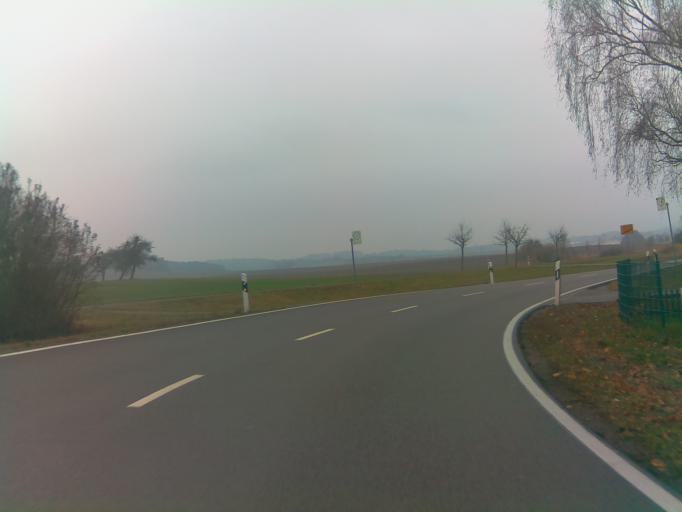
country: DE
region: Thuringia
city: Romhild
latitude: 50.4181
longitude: 10.5308
